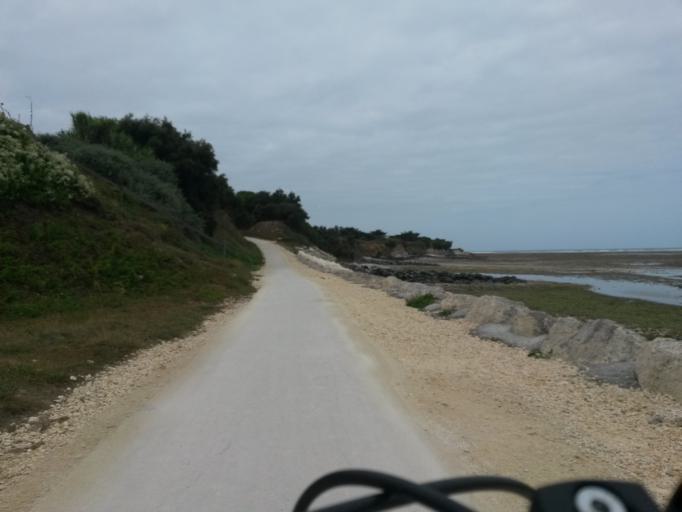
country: FR
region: Poitou-Charentes
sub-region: Departement de la Charente-Maritime
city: Saint-Denis-d'Oleron
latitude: 46.0445
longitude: -1.3974
